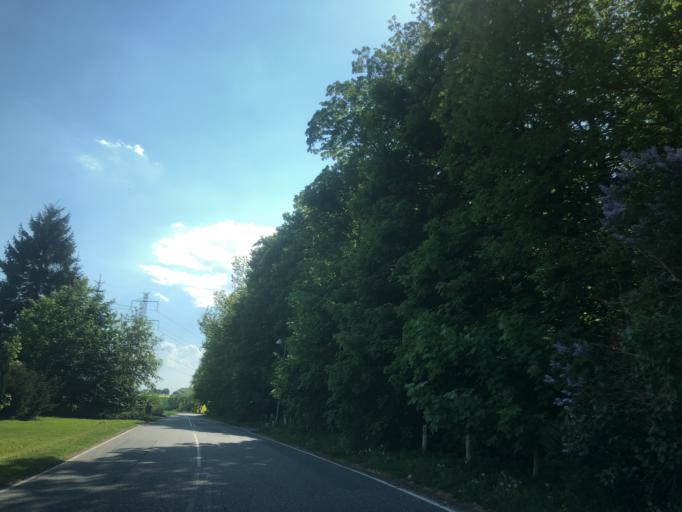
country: DK
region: Capital Region
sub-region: Hoje-Taastrup Kommune
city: Flong
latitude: 55.6302
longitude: 12.2224
